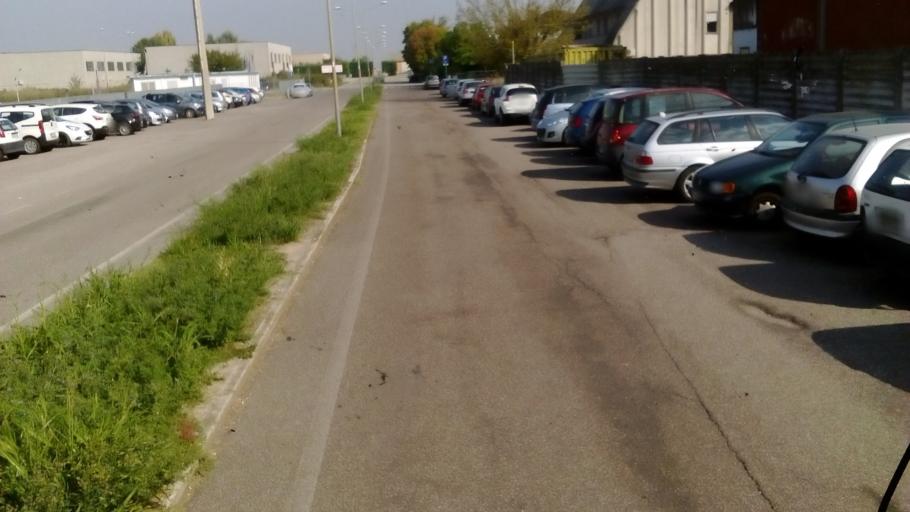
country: IT
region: Lombardy
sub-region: Provincia di Mantova
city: Ostiglia
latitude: 45.0909
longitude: 11.1381
